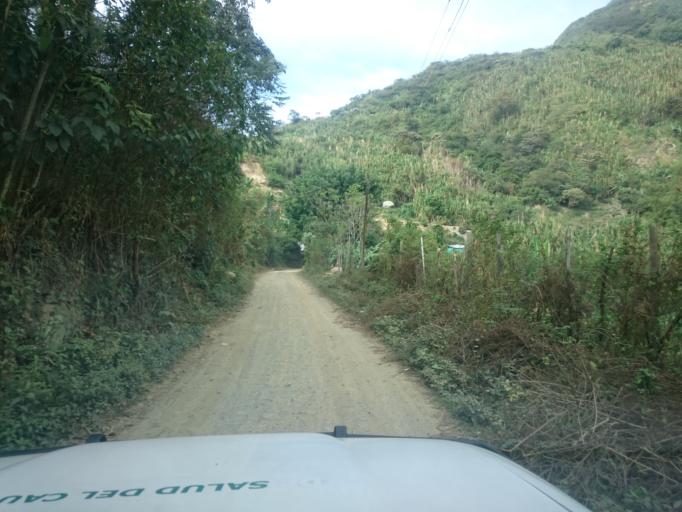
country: CO
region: Cauca
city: Suarez
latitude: 2.9304
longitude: -76.7161
